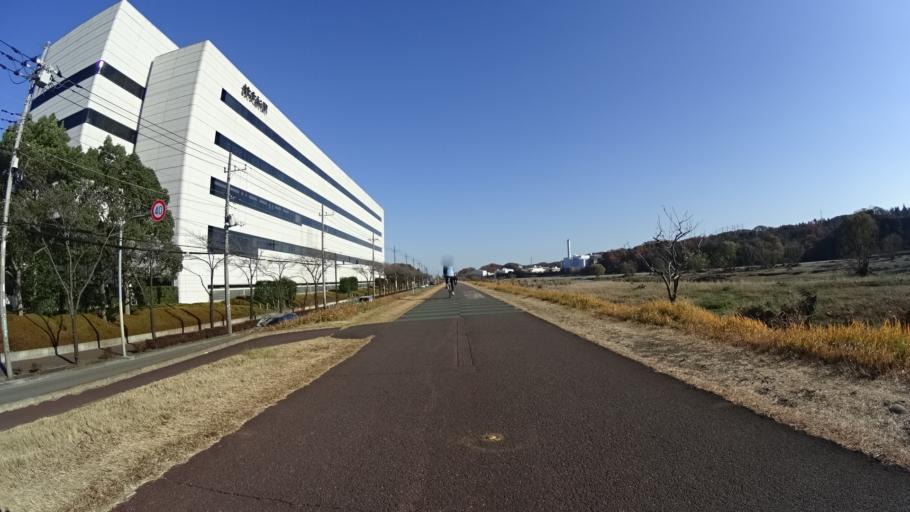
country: JP
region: Tokyo
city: Kokubunji
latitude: 35.6538
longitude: 139.4639
